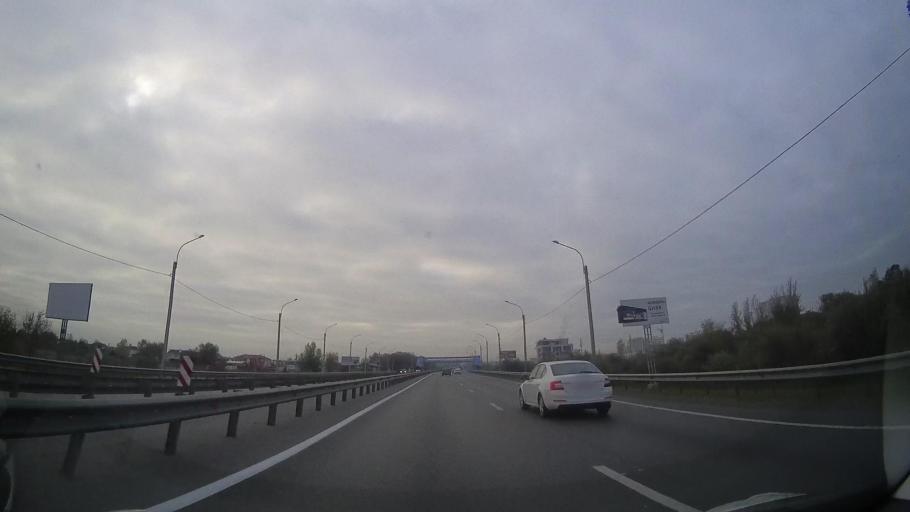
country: RU
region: Rostov
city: Bataysk
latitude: 47.1422
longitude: 39.7759
